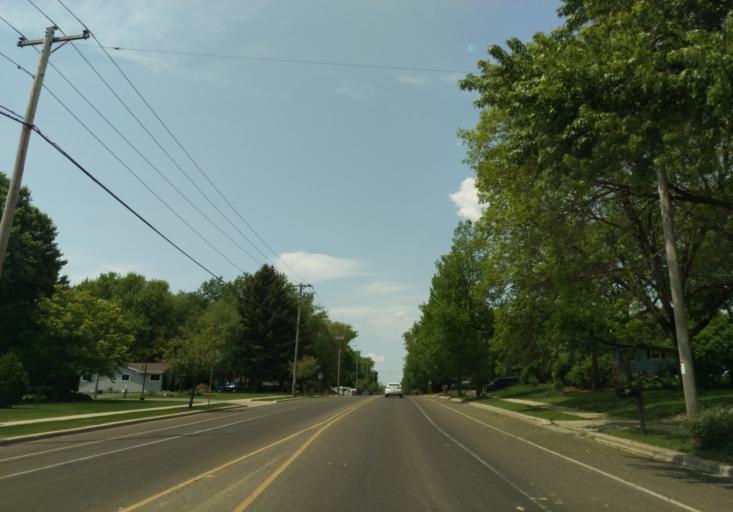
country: US
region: Wisconsin
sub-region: Dane County
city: Monona
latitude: 43.0735
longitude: -89.2920
